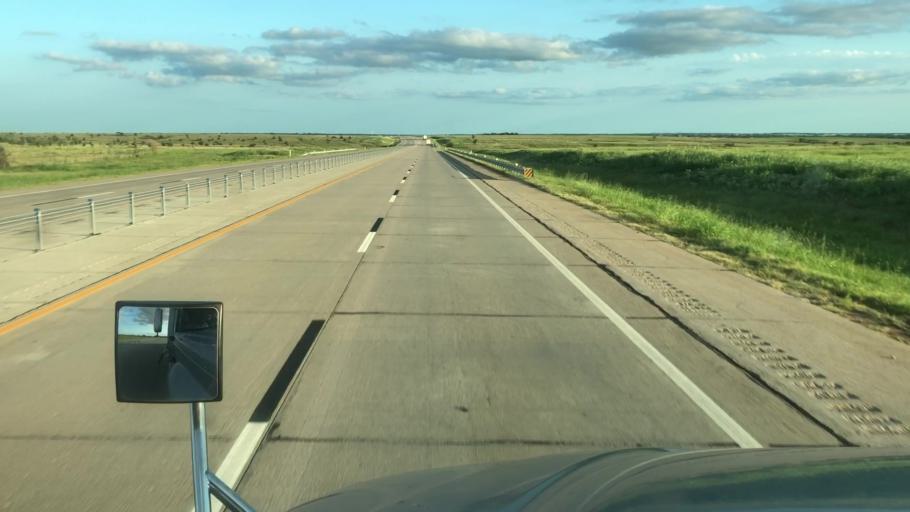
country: US
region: Oklahoma
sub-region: Pawnee County
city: Pawnee
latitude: 36.3562
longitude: -97.0315
